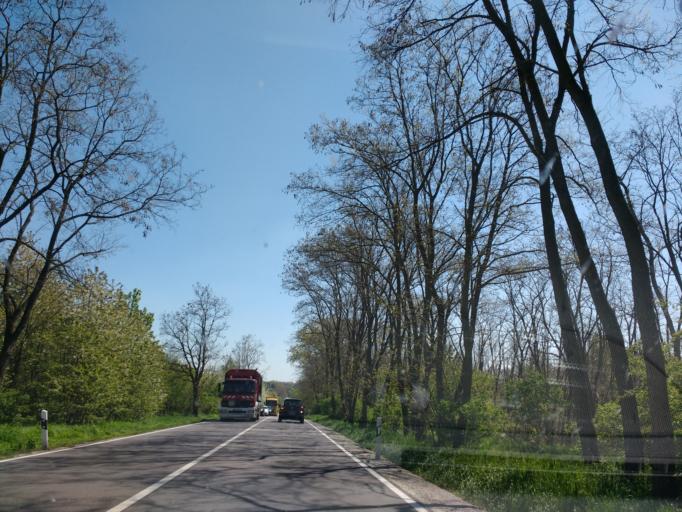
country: DE
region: Saxony-Anhalt
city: Deuben
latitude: 51.1240
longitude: 12.0663
